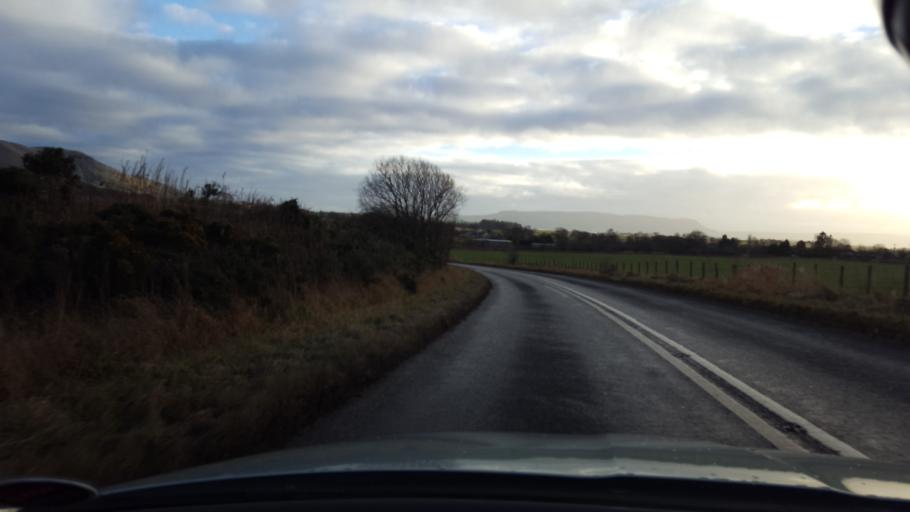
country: GB
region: Scotland
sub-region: Perth and Kinross
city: Milnathort
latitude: 56.2483
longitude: -3.3740
